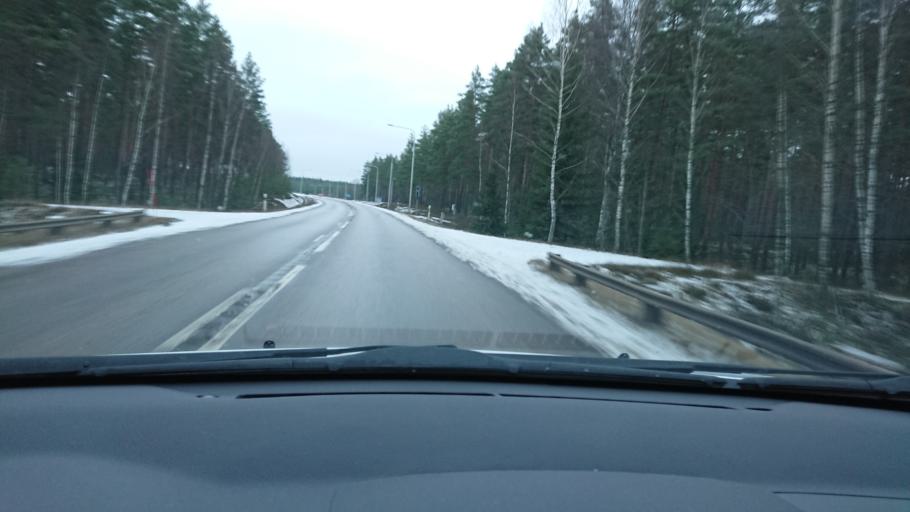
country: SE
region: Kalmar
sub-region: Hultsfreds Kommun
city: Hultsfred
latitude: 57.5152
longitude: 15.8412
